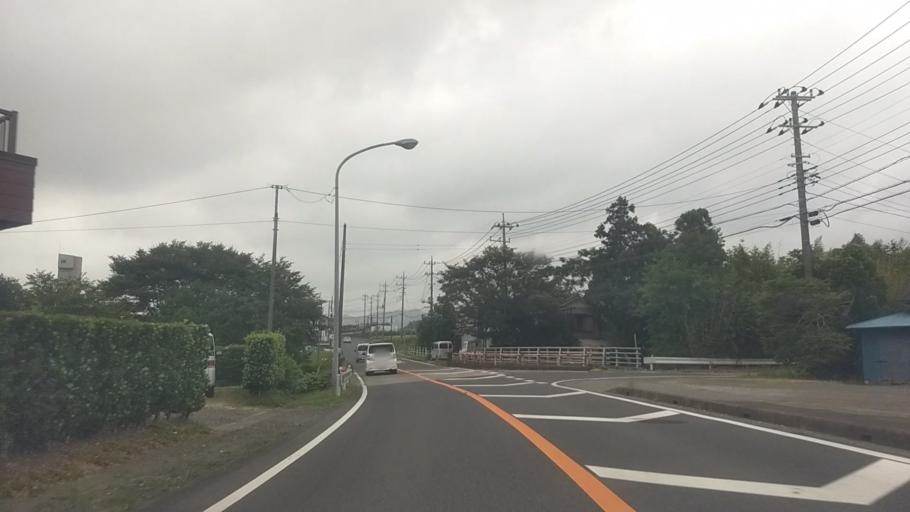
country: JP
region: Chiba
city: Kawaguchi
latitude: 35.1138
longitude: 140.0811
